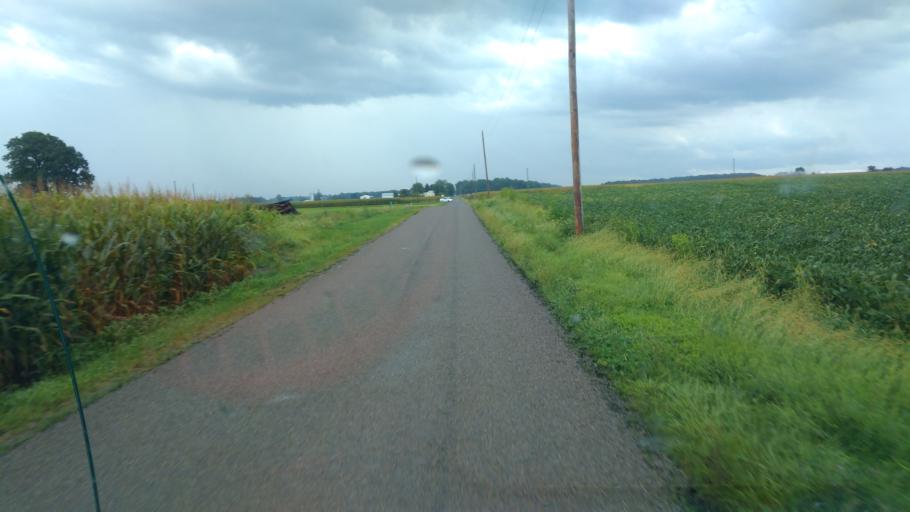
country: US
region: Ohio
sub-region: Hardin County
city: Kenton
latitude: 40.6886
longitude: -83.5979
